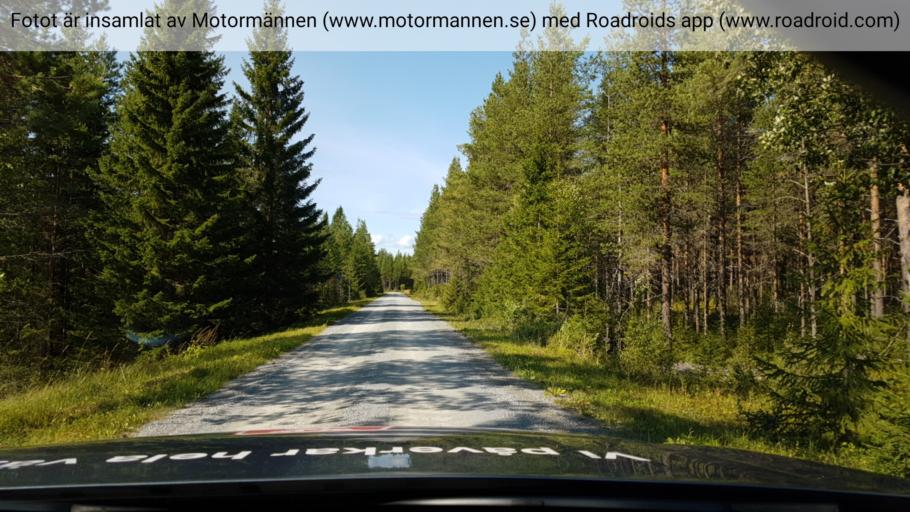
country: SE
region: Jaemtland
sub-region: OEstersunds Kommun
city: Ostersund
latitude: 63.1132
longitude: 14.5234
